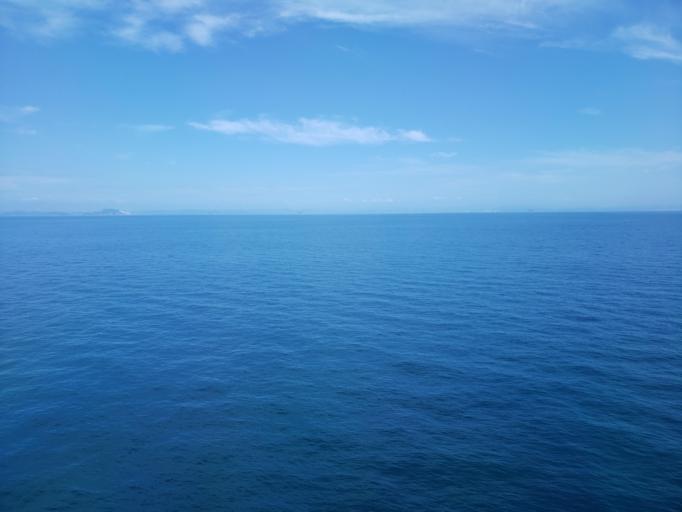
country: JP
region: Hyogo
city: Shirahamacho-usazakiminami
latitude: 34.5440
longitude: 134.7162
